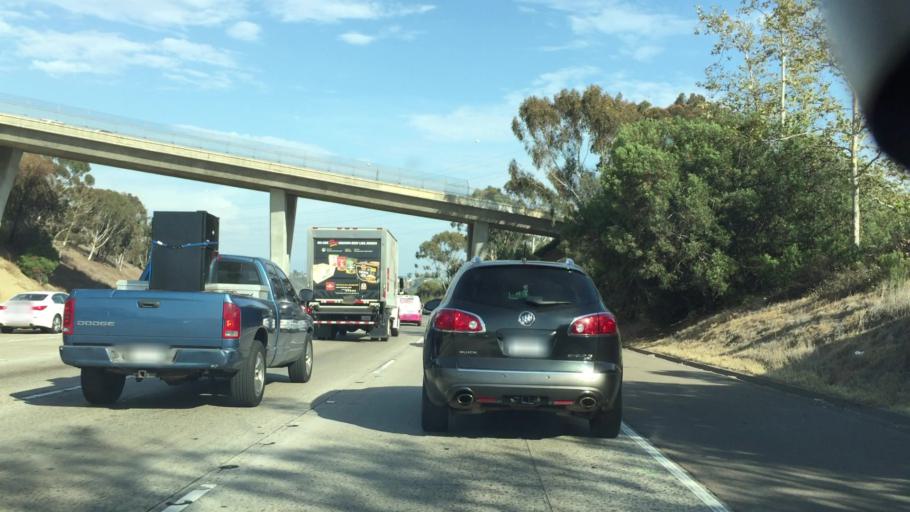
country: US
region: California
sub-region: San Diego County
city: San Diego
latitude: 32.7861
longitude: -117.1464
